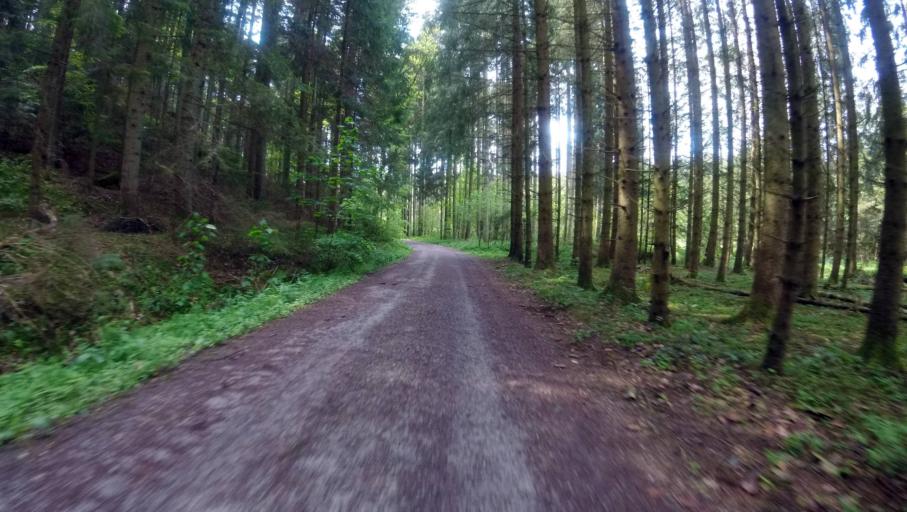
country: DE
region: Baden-Wuerttemberg
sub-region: Regierungsbezirk Stuttgart
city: Spraitbach
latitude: 48.8615
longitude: 9.7578
